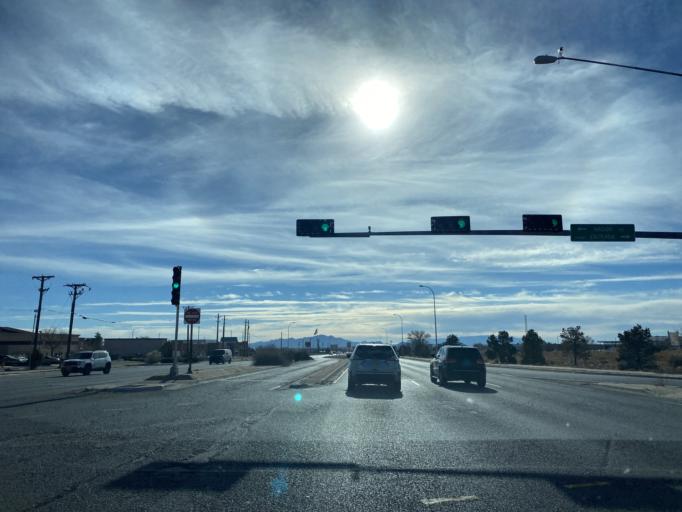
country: US
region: New Mexico
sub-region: Santa Fe County
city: Agua Fria
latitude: 35.6352
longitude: -106.0198
